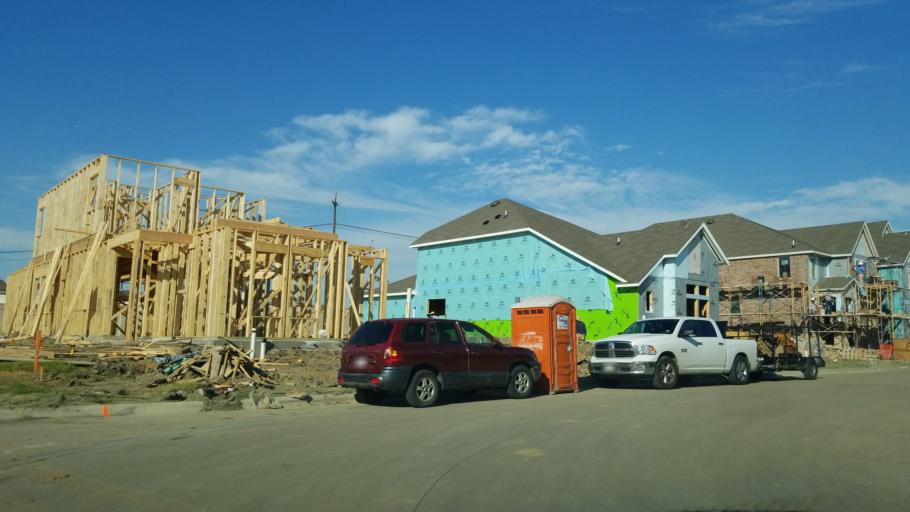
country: US
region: Texas
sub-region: Dallas County
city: Coppell
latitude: 32.9048
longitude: -96.9935
